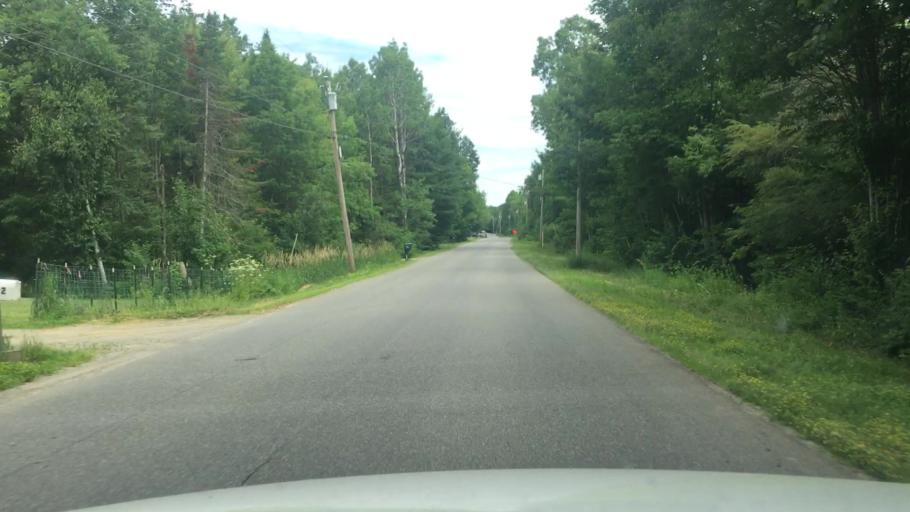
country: US
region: Maine
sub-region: Kennebec County
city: Clinton
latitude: 44.5979
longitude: -69.4719
